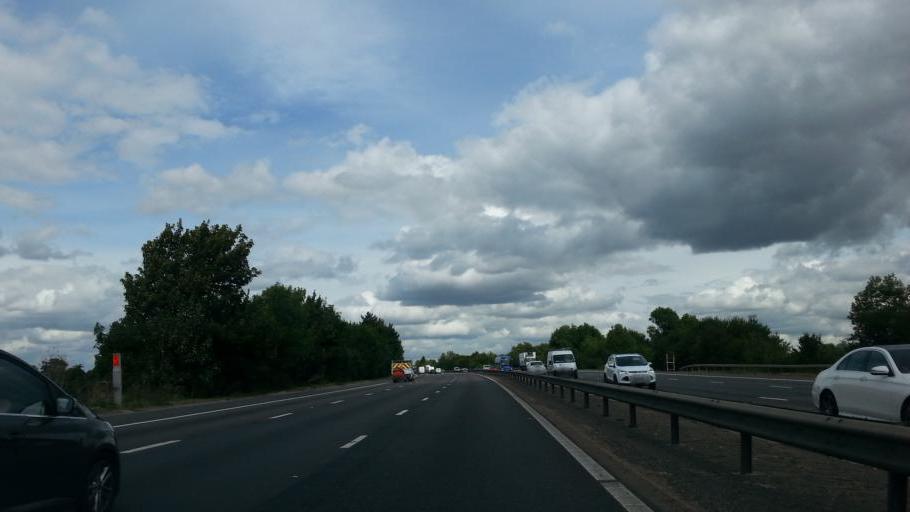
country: GB
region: England
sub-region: Essex
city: Little Hallingbury
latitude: 51.8122
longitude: 0.1807
